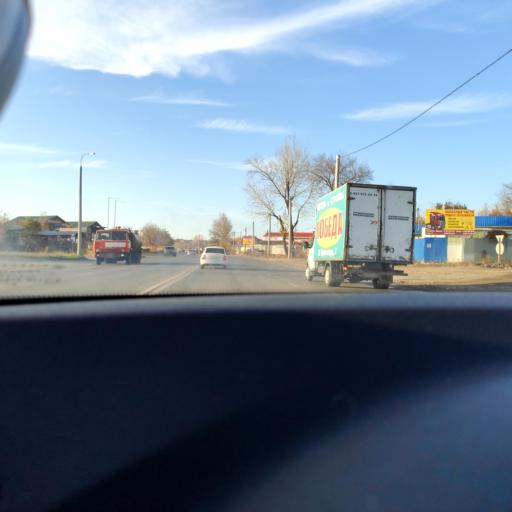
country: RU
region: Samara
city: Petra-Dubrava
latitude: 53.2674
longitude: 50.2816
